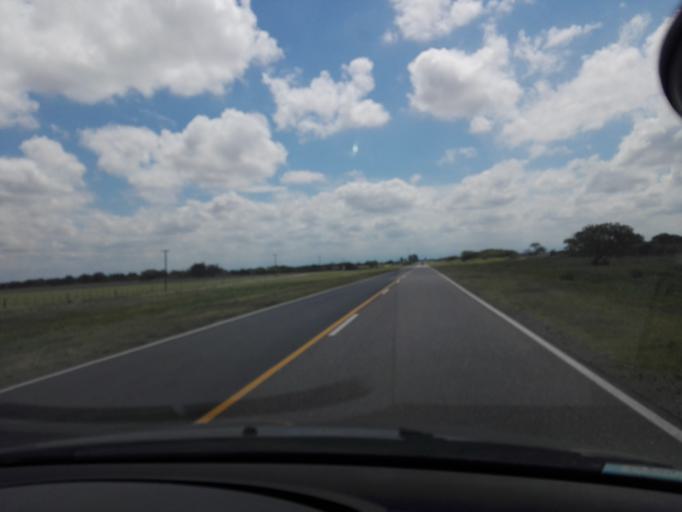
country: AR
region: Cordoba
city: Toledo
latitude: -31.6468
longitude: -64.0618
